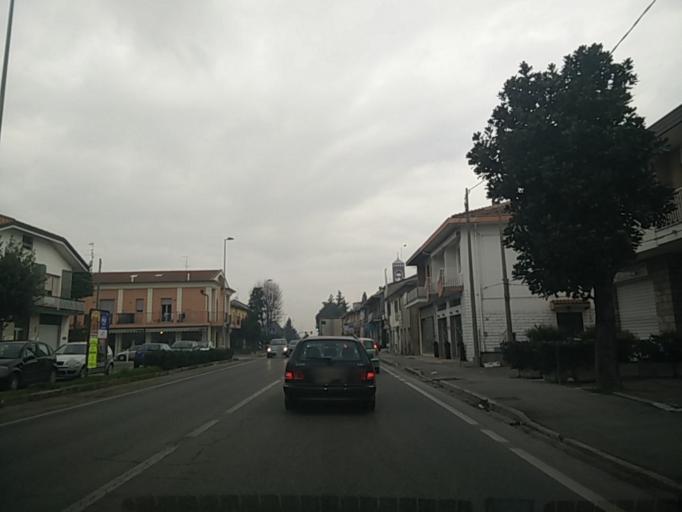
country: IT
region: Emilia-Romagna
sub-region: Provincia di Rimini
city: Santa Giustina
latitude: 44.0689
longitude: 12.4850
